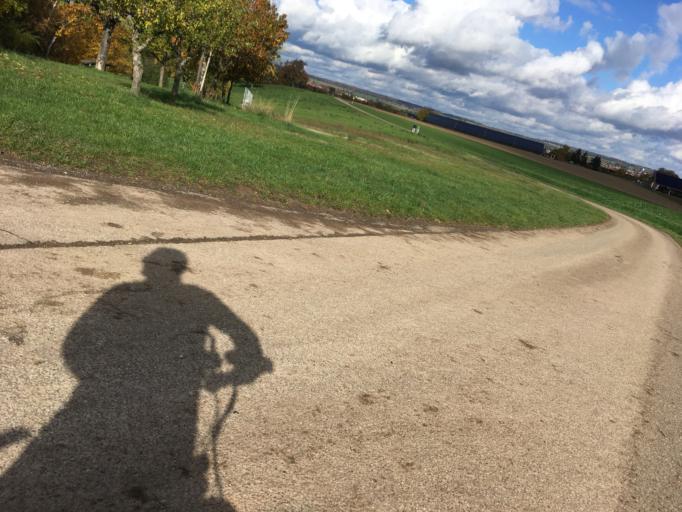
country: DE
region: Baden-Wuerttemberg
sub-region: Regierungsbezirk Stuttgart
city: Pfedelbach
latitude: 49.1739
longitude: 9.4918
